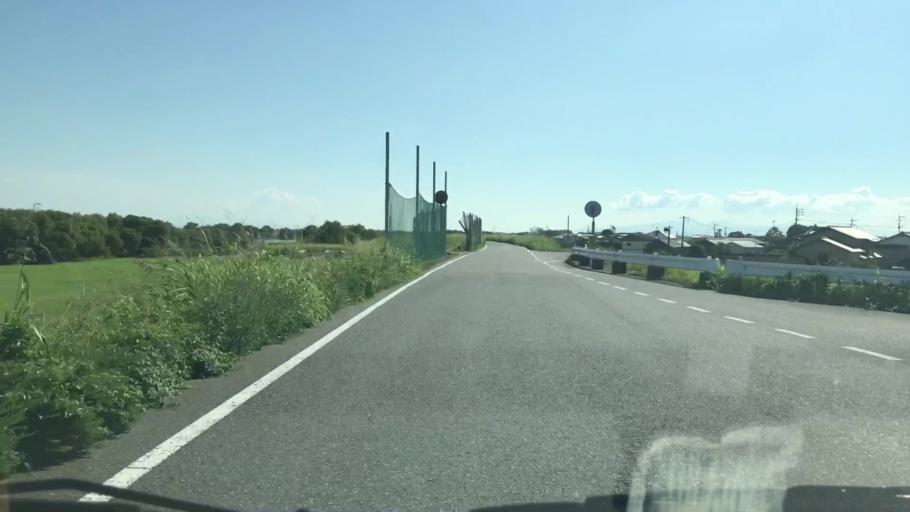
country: JP
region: Fukuoka
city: Kurume
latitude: 33.2822
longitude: 130.4491
